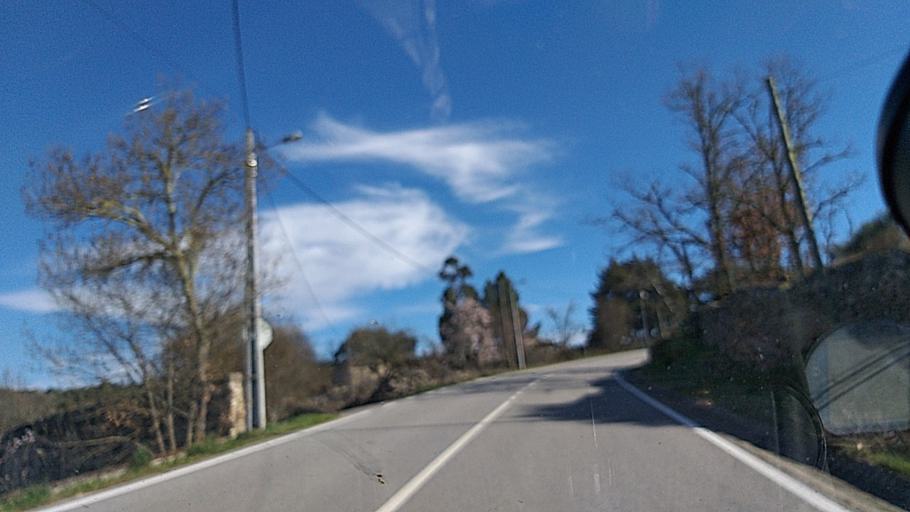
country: ES
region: Castille and Leon
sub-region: Provincia de Salamanca
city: Fuentes de Onoro
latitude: 40.6179
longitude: -6.8926
